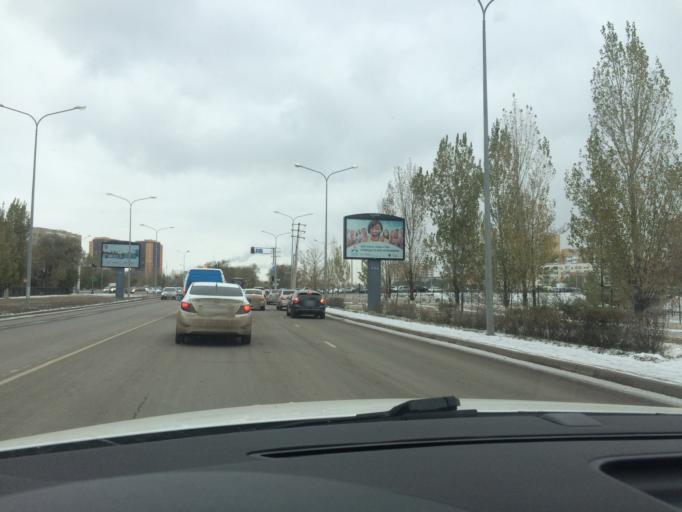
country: KZ
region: Astana Qalasy
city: Astana
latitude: 51.1602
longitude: 71.4670
